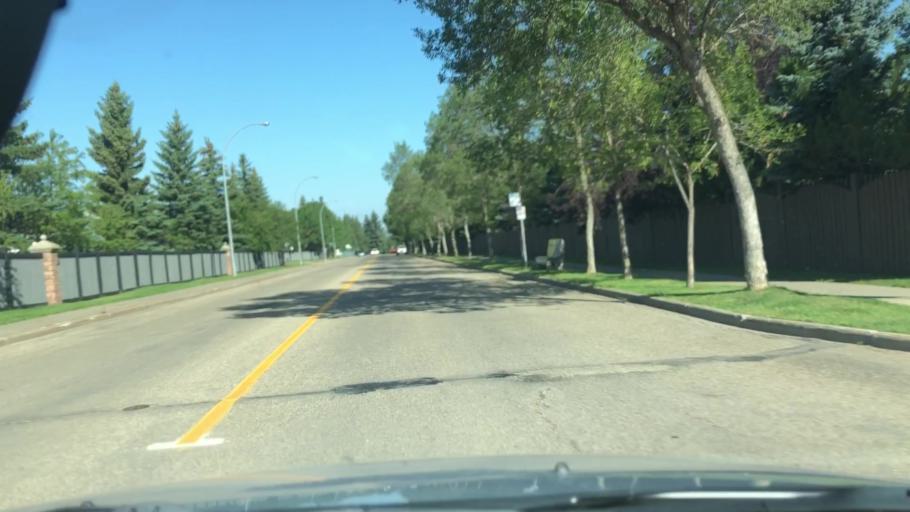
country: CA
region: Alberta
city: Edmonton
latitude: 53.4746
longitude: -113.5987
